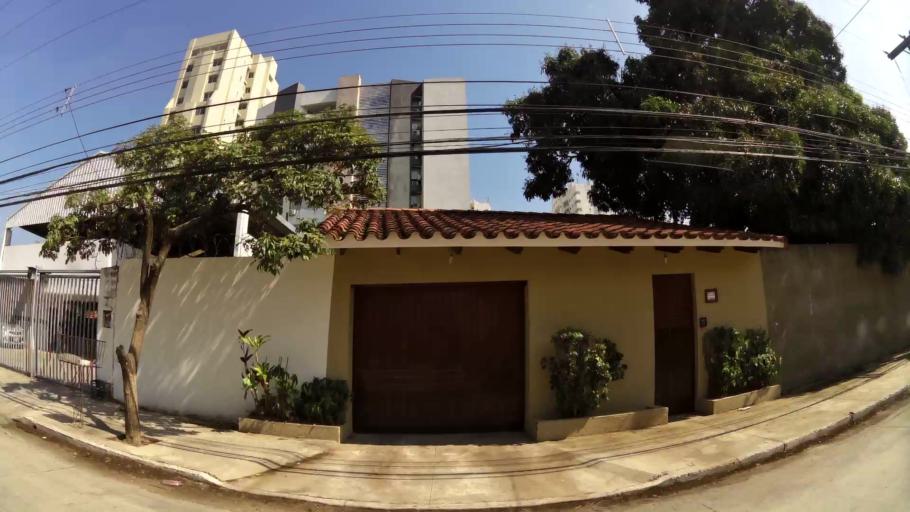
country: BO
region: Santa Cruz
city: Santa Cruz de la Sierra
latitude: -17.7491
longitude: -63.1675
